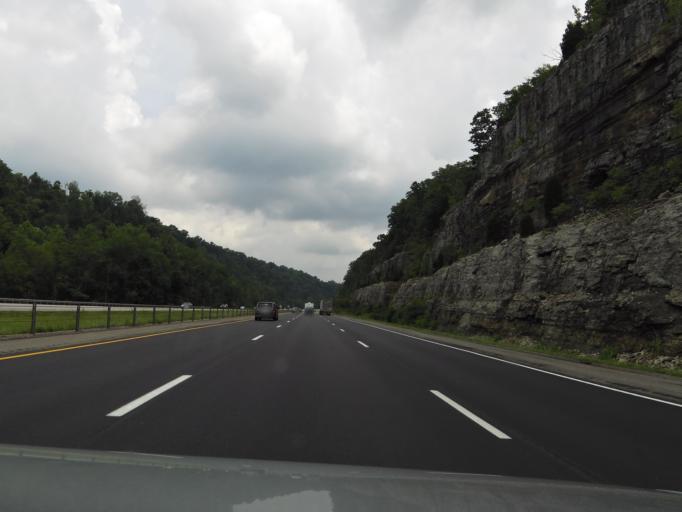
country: US
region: Kentucky
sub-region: Hardin County
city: Elizabethtown
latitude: 37.7494
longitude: -85.7946
